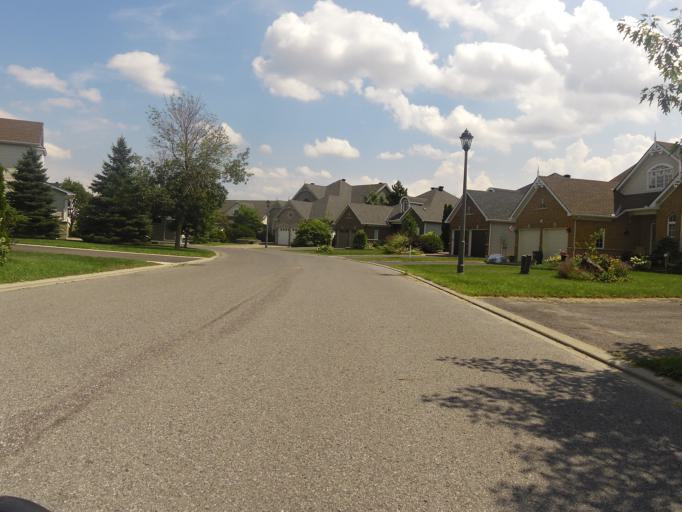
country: CA
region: Ontario
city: Bells Corners
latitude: 45.3108
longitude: -75.9245
